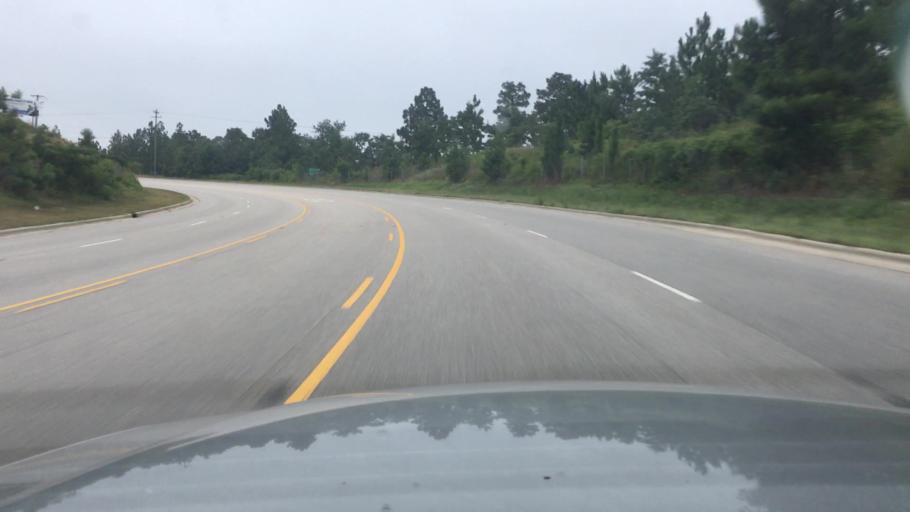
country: US
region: North Carolina
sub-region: Cumberland County
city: Fayetteville
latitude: 35.0136
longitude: -78.8890
